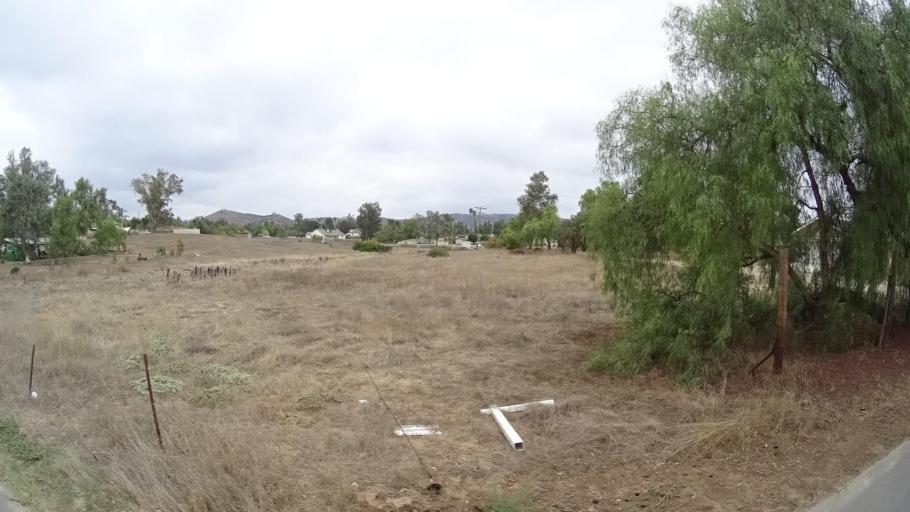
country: US
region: California
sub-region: San Diego County
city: Ramona
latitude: 33.0290
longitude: -116.8579
